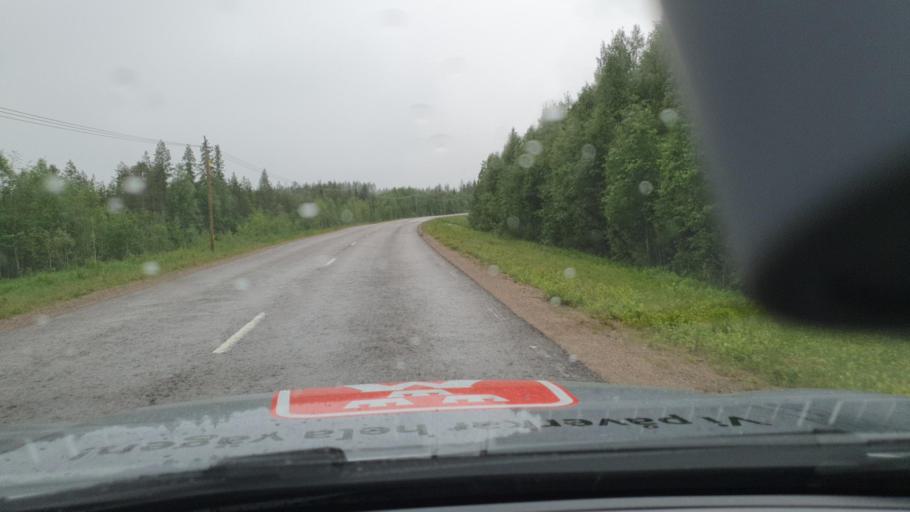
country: SE
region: Norrbotten
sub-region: Overkalix Kommun
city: OEverkalix
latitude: 66.4416
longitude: 23.0370
